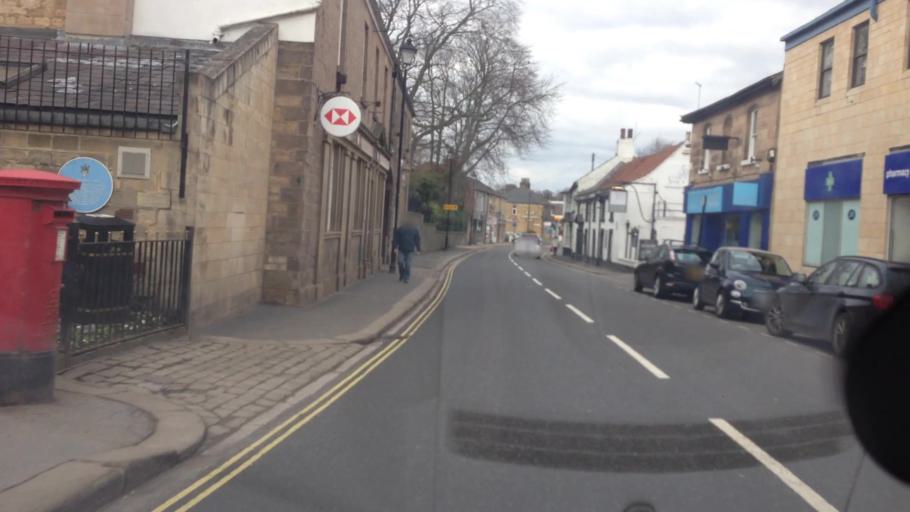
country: GB
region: England
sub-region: City and Borough of Leeds
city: Wetherby
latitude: 53.9290
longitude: -1.3854
